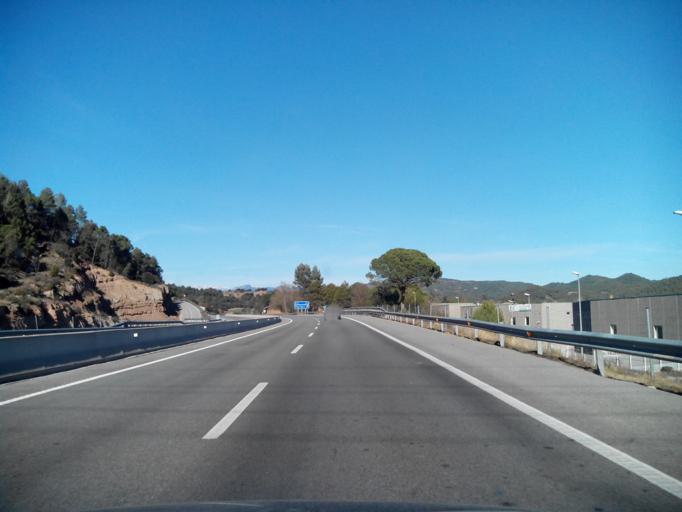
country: ES
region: Catalonia
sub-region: Provincia de Barcelona
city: Puig-reig
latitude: 41.9384
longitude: 1.8770
